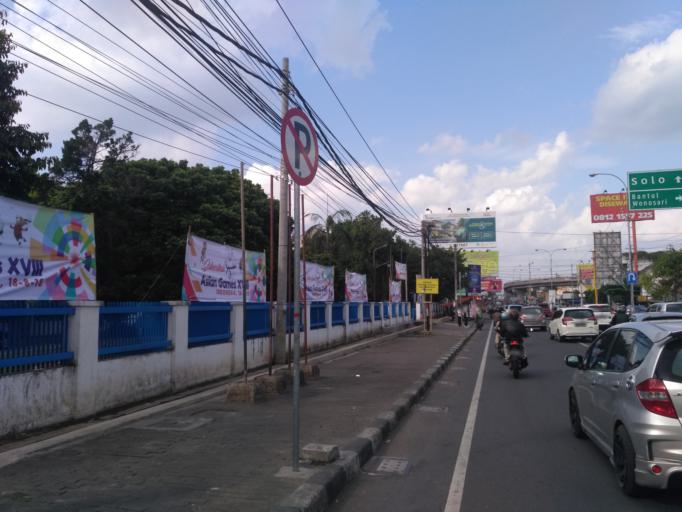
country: ID
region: Daerah Istimewa Yogyakarta
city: Depok
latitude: -7.7833
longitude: 110.4088
